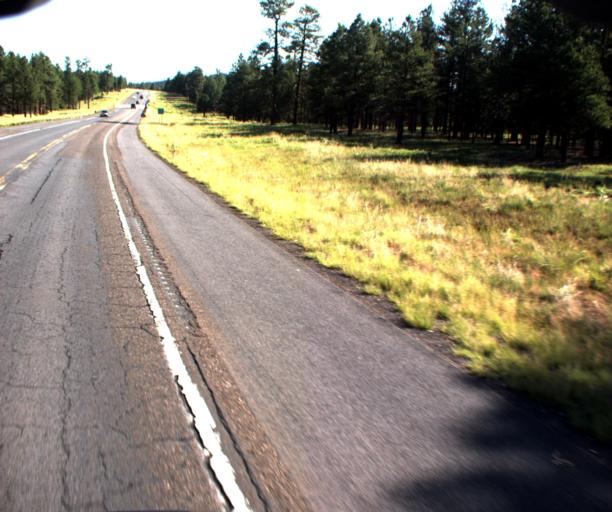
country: US
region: Arizona
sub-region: Coconino County
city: Williams
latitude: 35.2837
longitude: -112.1456
